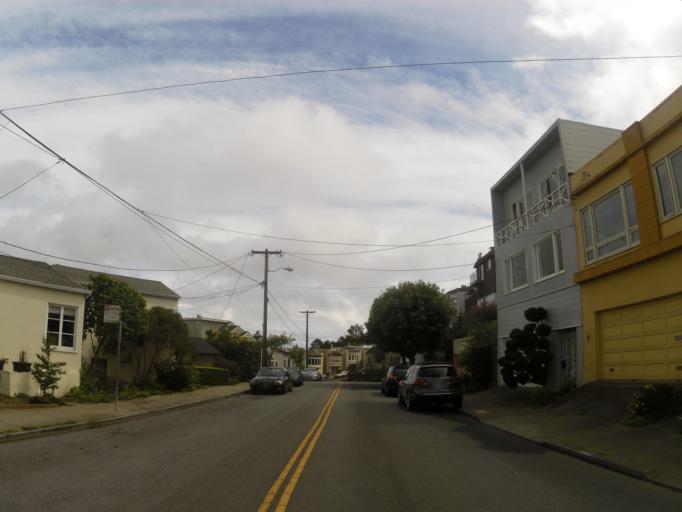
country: US
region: California
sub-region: San Mateo County
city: Daly City
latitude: 37.7515
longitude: -122.4674
